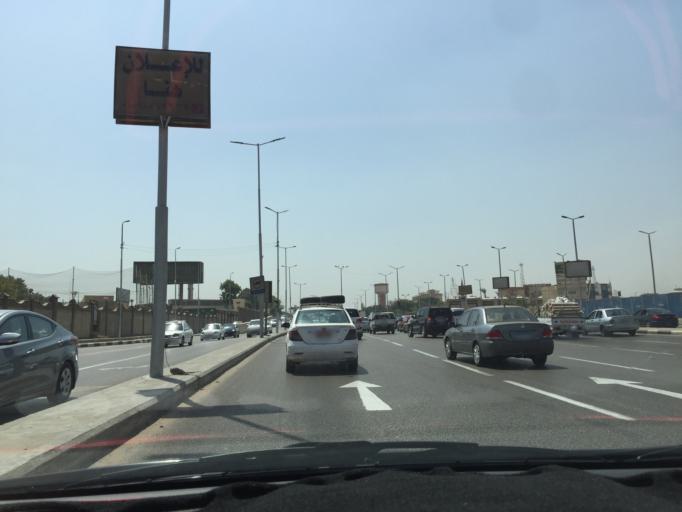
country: EG
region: Muhafazat al Qahirah
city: Cairo
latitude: 30.0583
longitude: 31.2820
